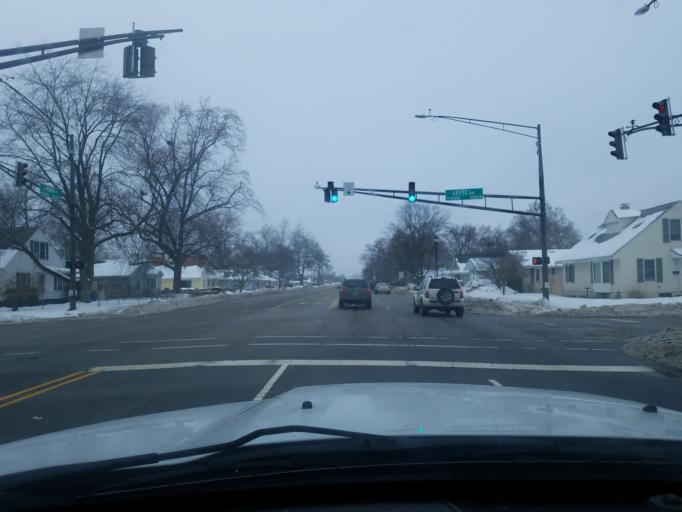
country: US
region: Indiana
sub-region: Saint Joseph County
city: Mishawaka
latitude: 41.6839
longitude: -86.1815
